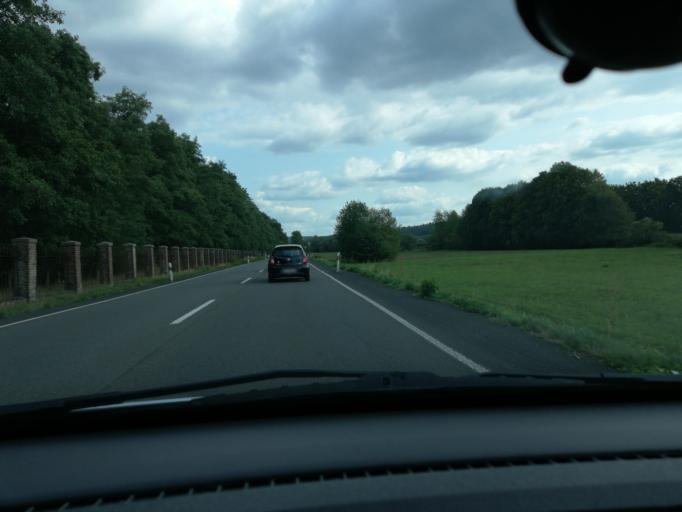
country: DE
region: North Rhine-Westphalia
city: Wetter (Ruhr)
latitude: 51.4029
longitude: 7.3566
